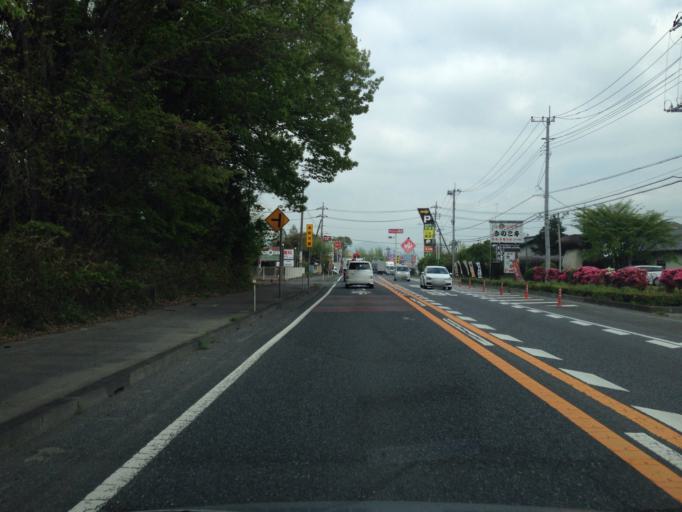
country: JP
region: Ibaraki
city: Iwase
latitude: 36.3480
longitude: 140.0501
